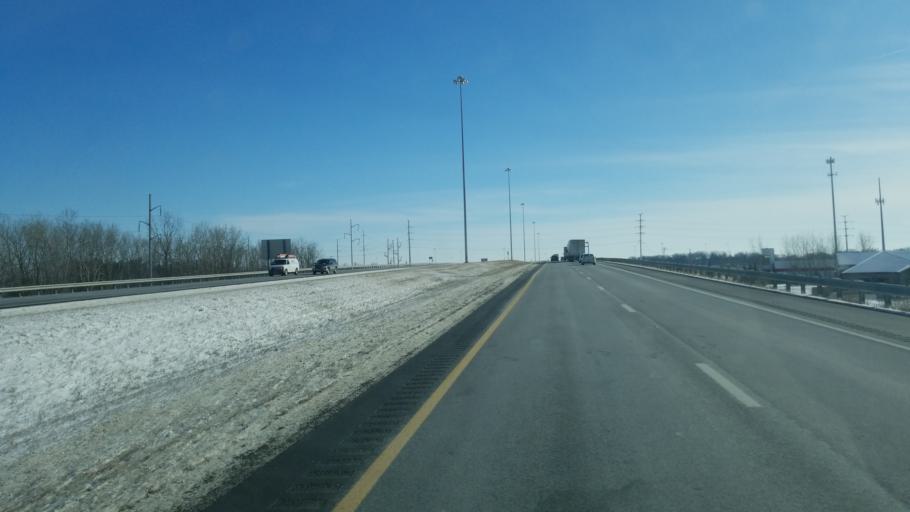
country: US
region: Ohio
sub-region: Lucas County
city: Maumee
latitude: 41.5622
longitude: -83.6893
